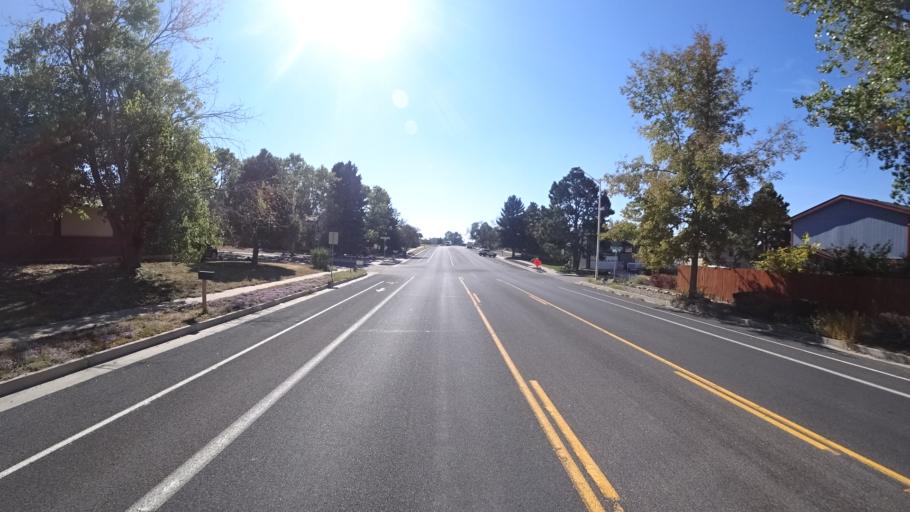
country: US
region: Colorado
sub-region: El Paso County
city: Cimarron Hills
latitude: 38.9187
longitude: -104.7655
